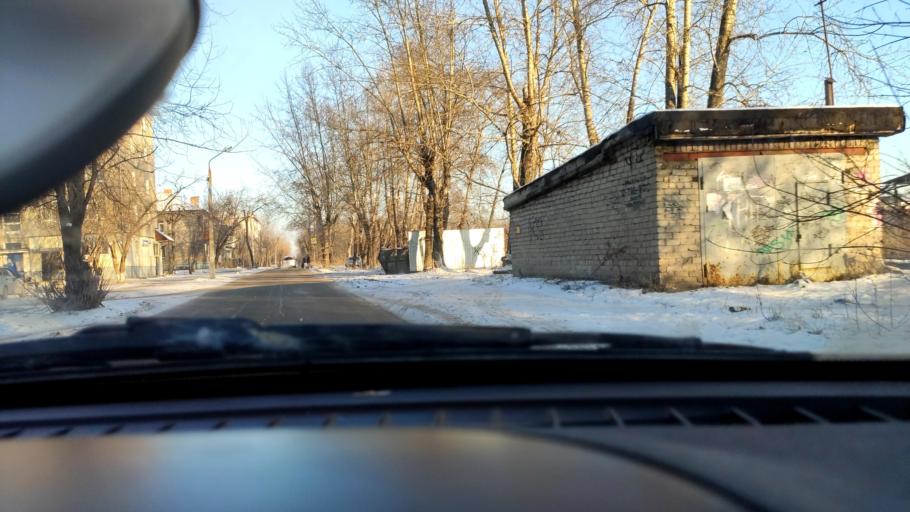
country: RU
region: Perm
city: Overyata
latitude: 58.0005
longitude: 55.9307
